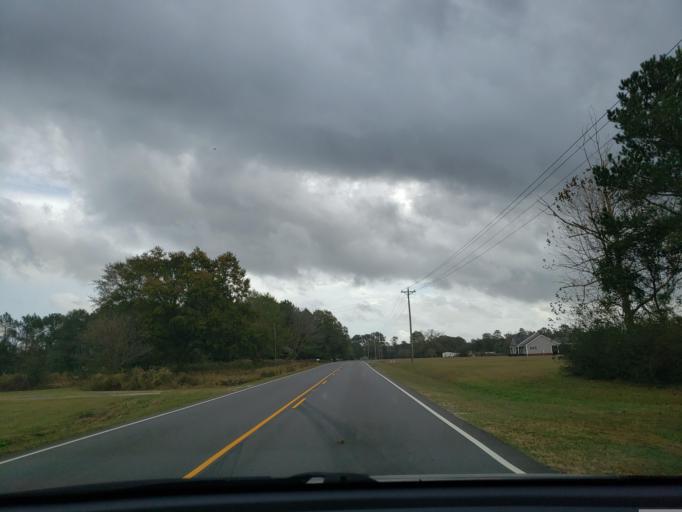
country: US
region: North Carolina
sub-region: Duplin County
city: Kenansville
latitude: 34.8706
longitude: -77.8877
